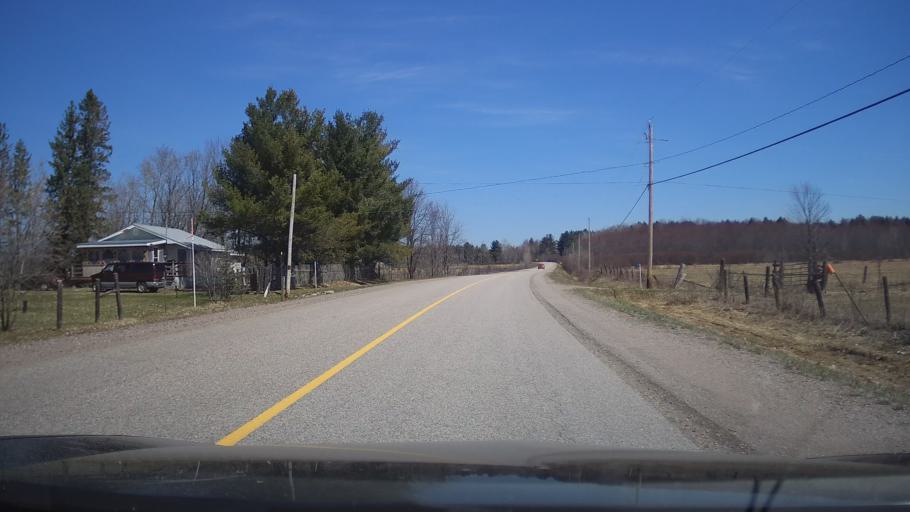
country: CA
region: Ontario
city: Arnprior
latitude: 45.5383
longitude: -76.3684
